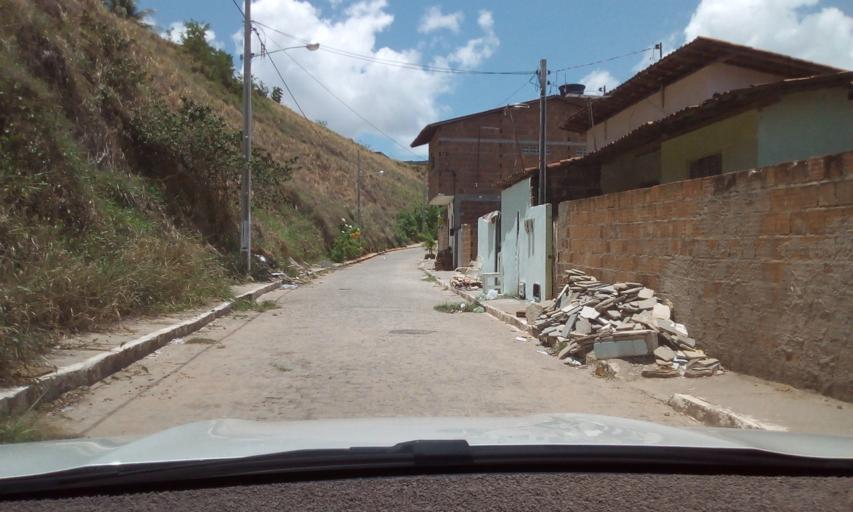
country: BR
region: Paraiba
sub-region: Joao Pessoa
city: Joao Pessoa
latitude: -7.1487
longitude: -34.8281
